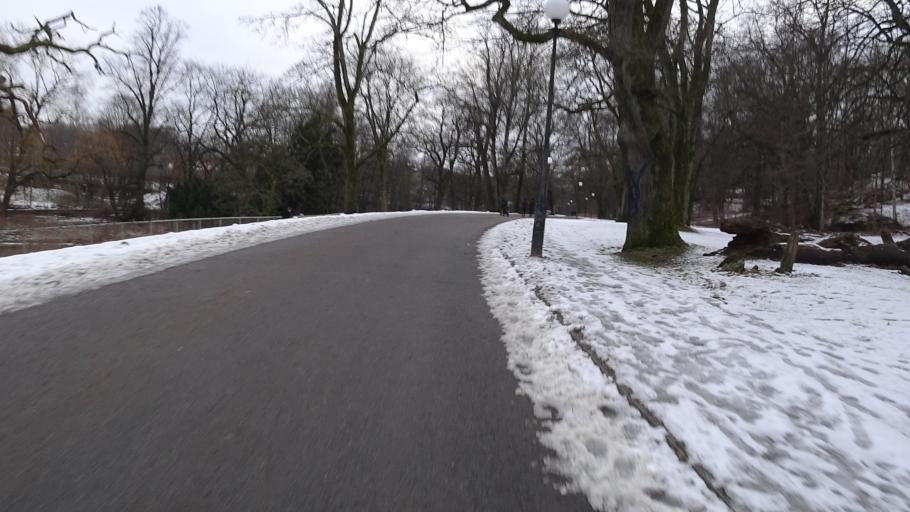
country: SE
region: Vaestra Goetaland
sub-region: Goteborg
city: Goeteborg
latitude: 57.6873
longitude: 11.9511
